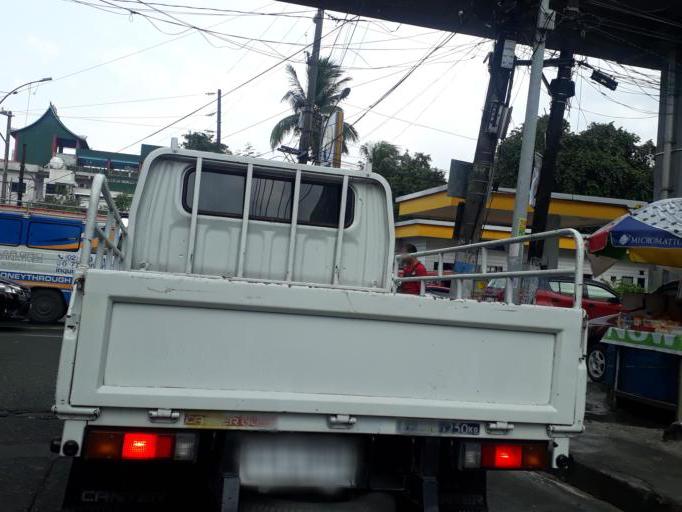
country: PH
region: Metro Manila
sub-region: San Juan
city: San Juan
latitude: 14.6186
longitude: 121.0433
